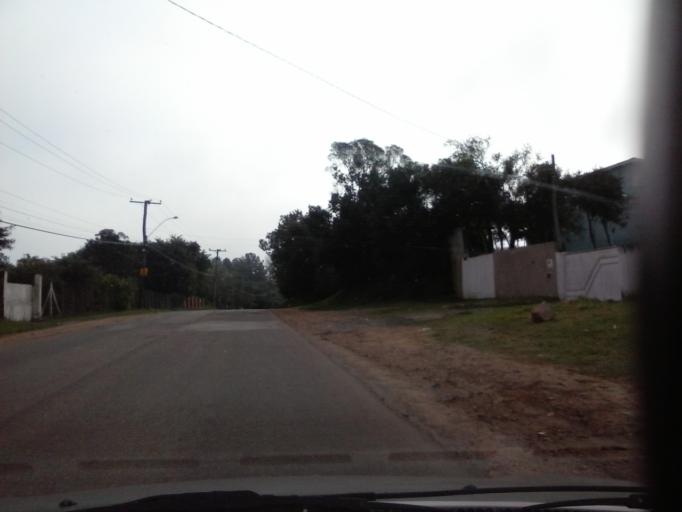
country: BR
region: Rio Grande do Sul
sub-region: Viamao
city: Viamao
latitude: -30.0597
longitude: -51.0582
